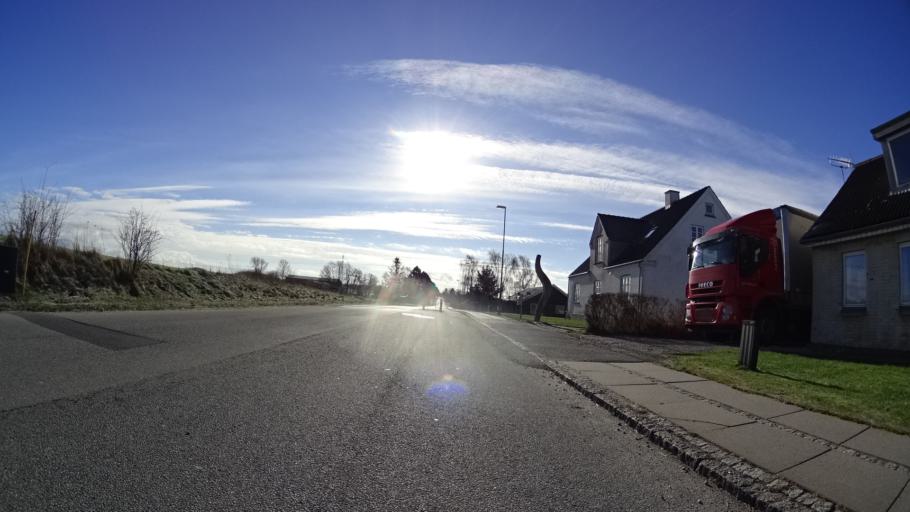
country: DK
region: Central Jutland
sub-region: Arhus Kommune
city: Kolt
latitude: 56.1255
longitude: 10.0641
